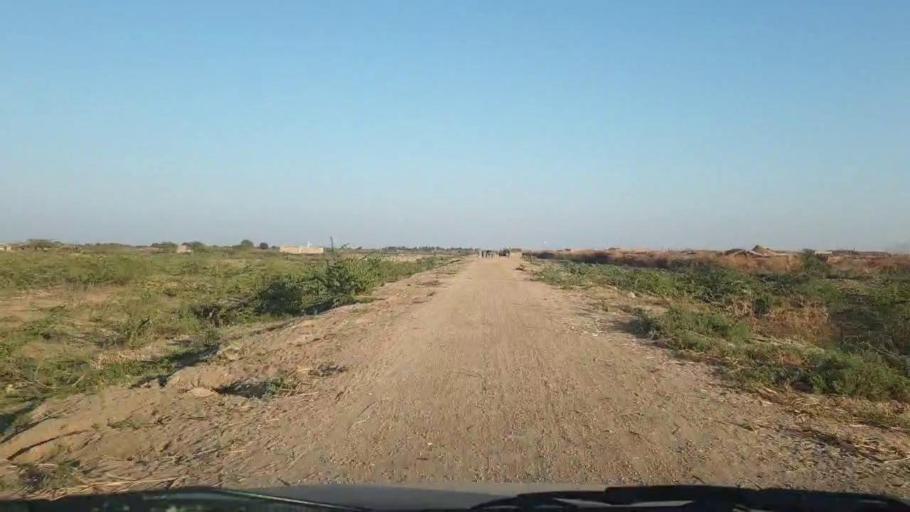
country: PK
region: Sindh
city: Samaro
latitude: 25.3221
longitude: 69.2907
